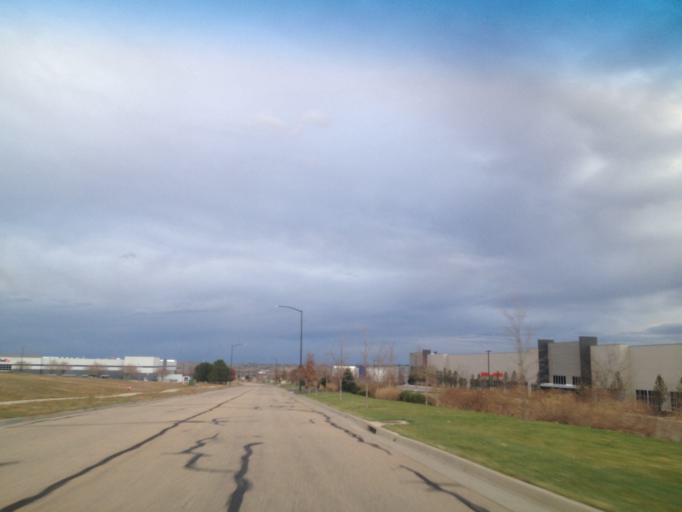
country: US
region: Colorado
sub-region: Boulder County
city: Louisville
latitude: 39.9710
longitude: -105.1156
